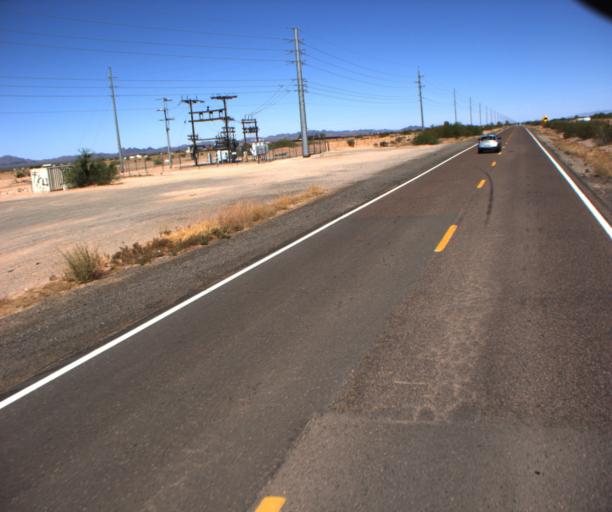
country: US
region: Arizona
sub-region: La Paz County
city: Salome
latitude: 33.8511
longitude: -113.9044
